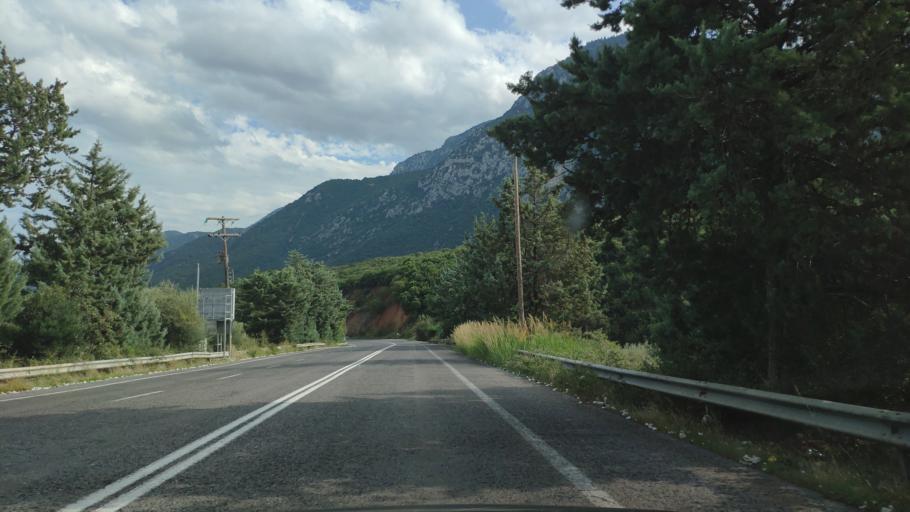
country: GR
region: Central Greece
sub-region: Nomos Fthiotidos
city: Anthili
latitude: 38.7989
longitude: 22.5066
